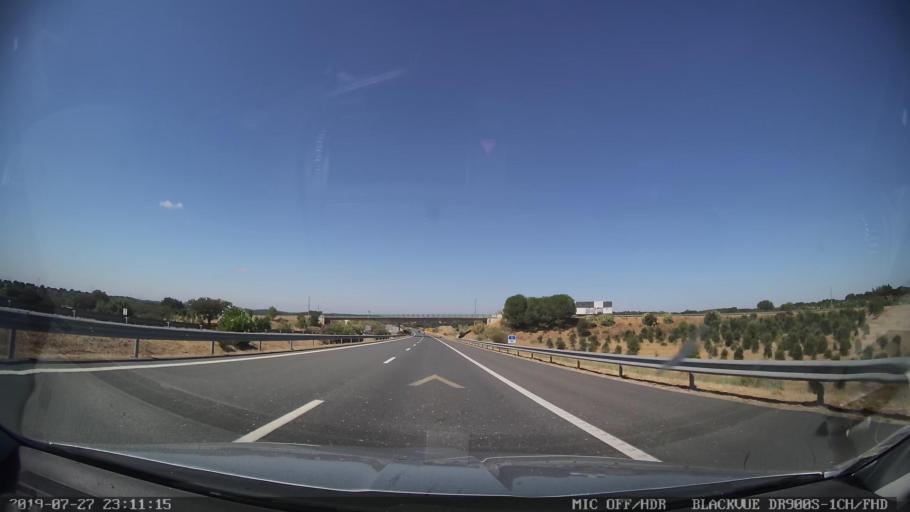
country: PT
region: Evora
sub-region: Estremoz
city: Estremoz
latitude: 38.7521
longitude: -7.7244
